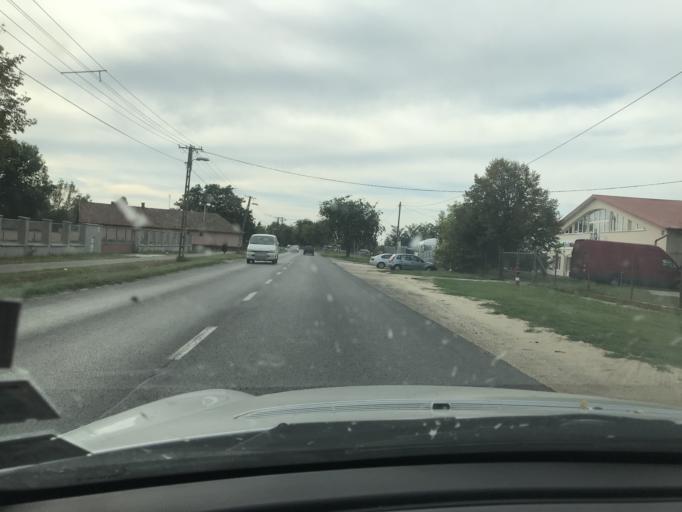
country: HU
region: Bacs-Kiskun
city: Kecel
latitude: 46.5202
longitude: 19.2313
